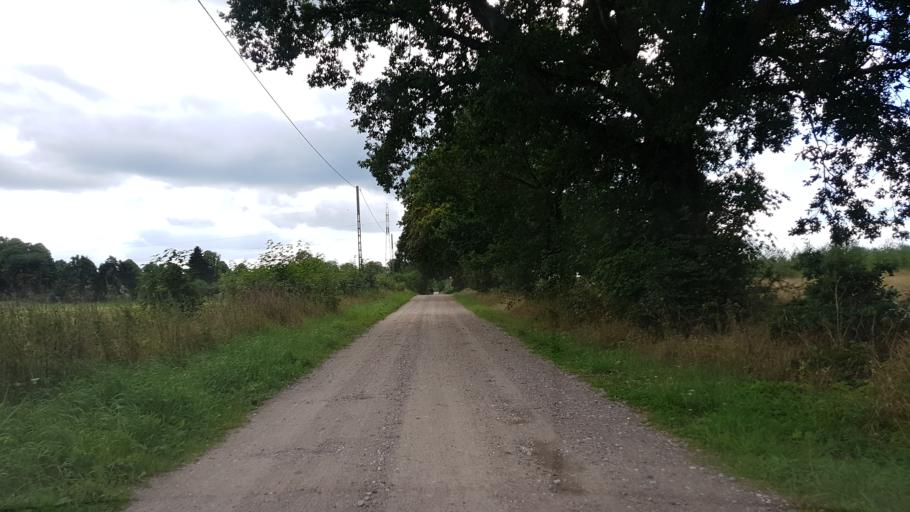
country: PL
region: West Pomeranian Voivodeship
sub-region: Powiat bialogardzki
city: Tychowo
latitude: 53.9974
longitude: 16.3049
